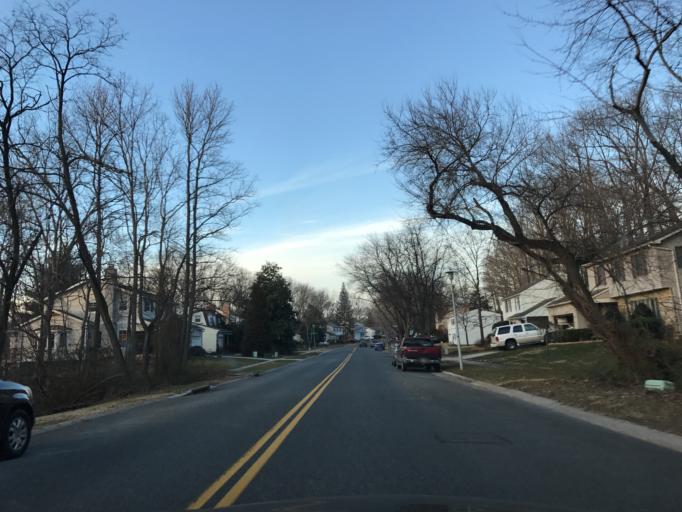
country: US
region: Maryland
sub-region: Harford County
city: Edgewood
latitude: 39.4028
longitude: -76.3445
